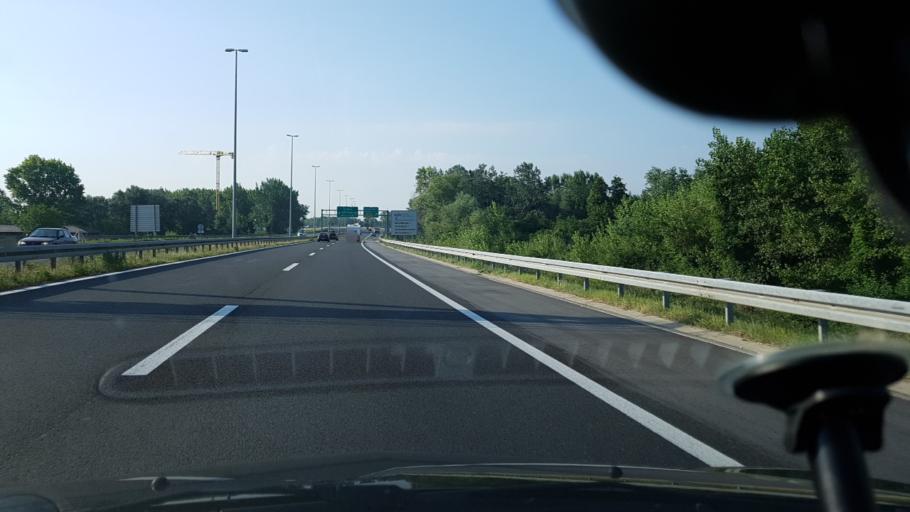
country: HR
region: Grad Zagreb
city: Jezdovec
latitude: 45.7947
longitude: 15.8455
